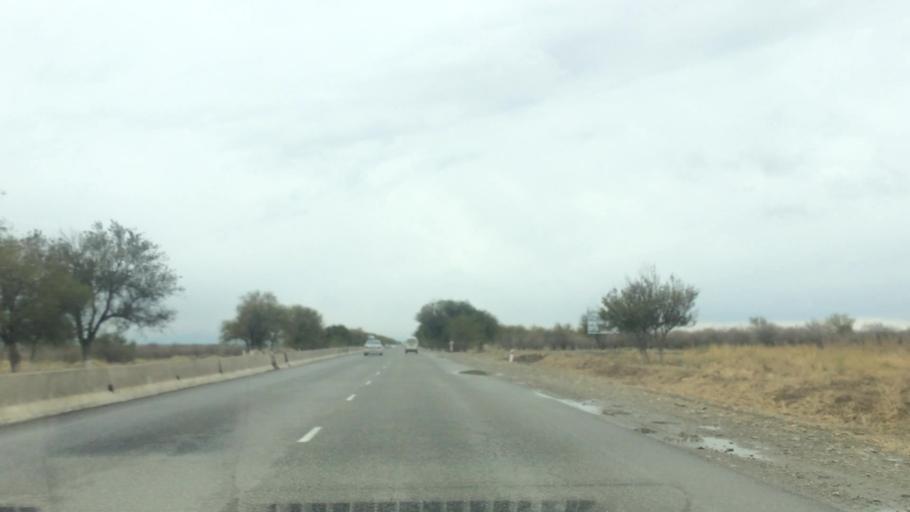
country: UZ
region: Samarqand
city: Bulung'ur
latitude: 39.8152
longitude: 67.3767
